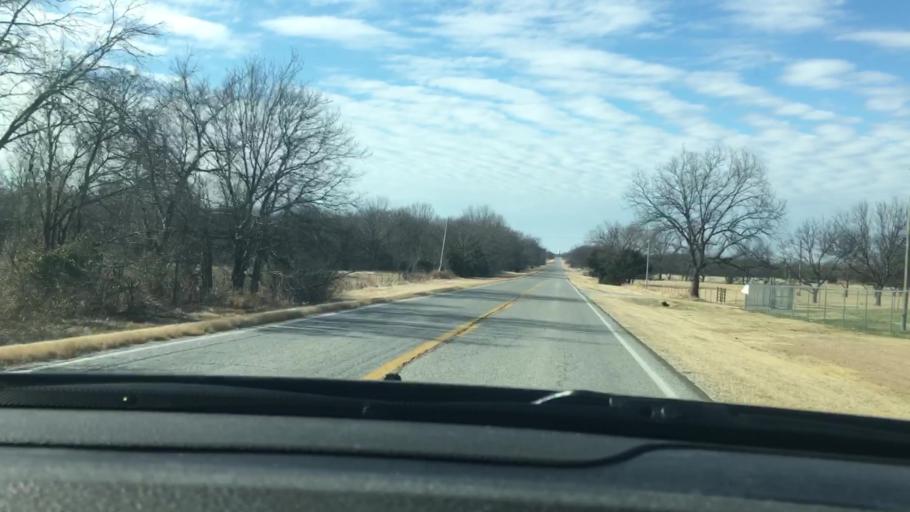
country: US
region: Oklahoma
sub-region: Garvin County
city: Wynnewood
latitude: 34.6516
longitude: -97.1221
